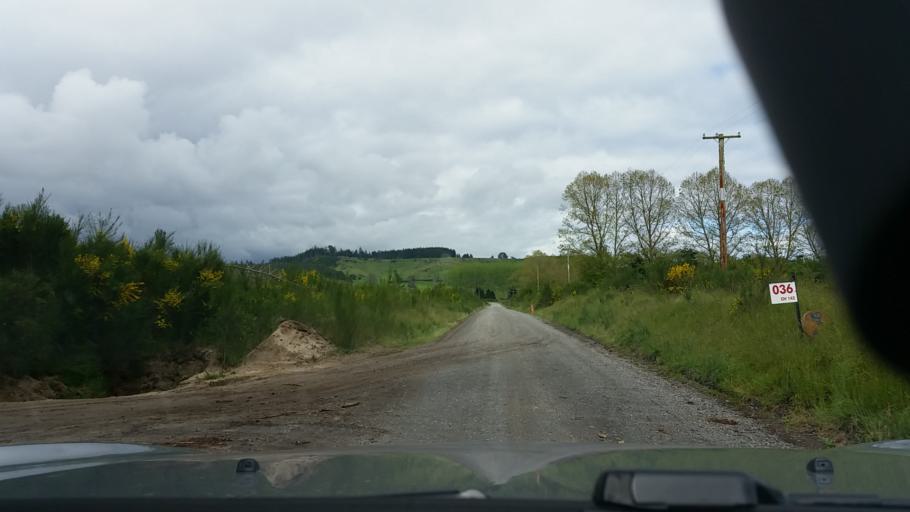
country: NZ
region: Bay of Plenty
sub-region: Whakatane District
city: Murupara
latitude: -38.3362
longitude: 176.5595
